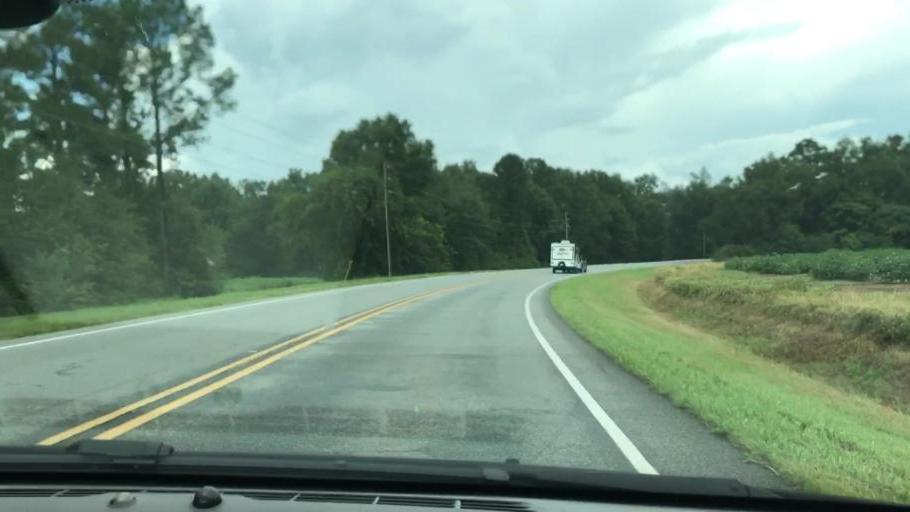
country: US
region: Georgia
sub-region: Early County
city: Blakely
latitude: 31.3864
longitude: -84.9570
